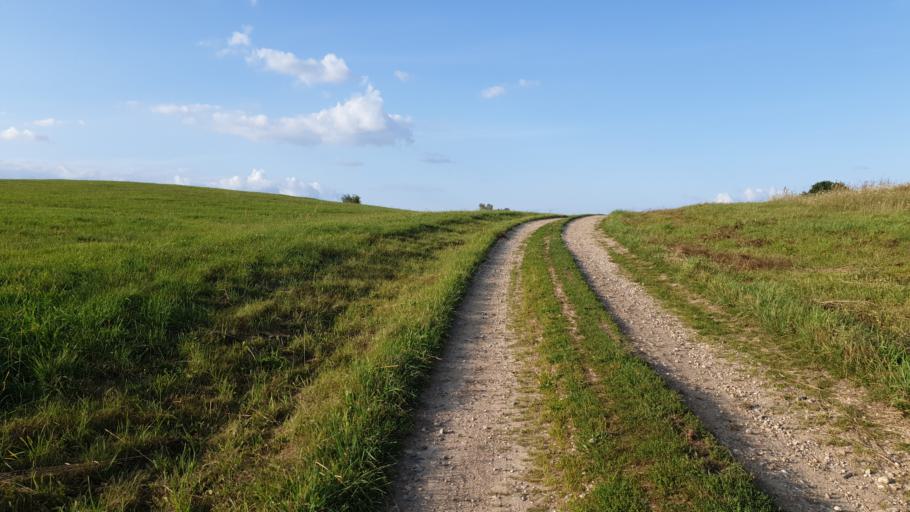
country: LT
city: Grigiskes
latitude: 54.7714
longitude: 25.0311
